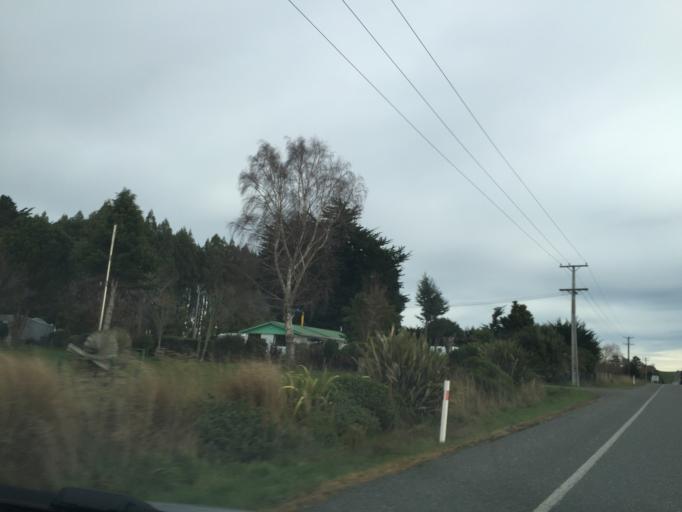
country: NZ
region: Southland
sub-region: Gore District
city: Gore
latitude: -46.3094
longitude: 168.7598
